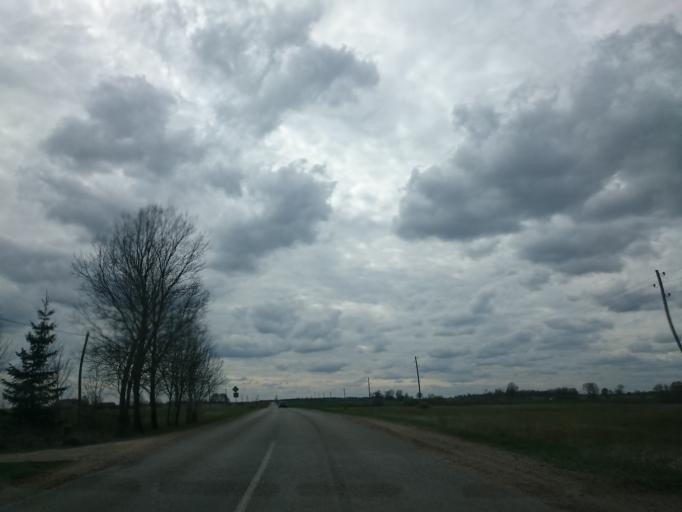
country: LV
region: Talsu Rajons
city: Sabile
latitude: 56.9594
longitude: 22.6142
